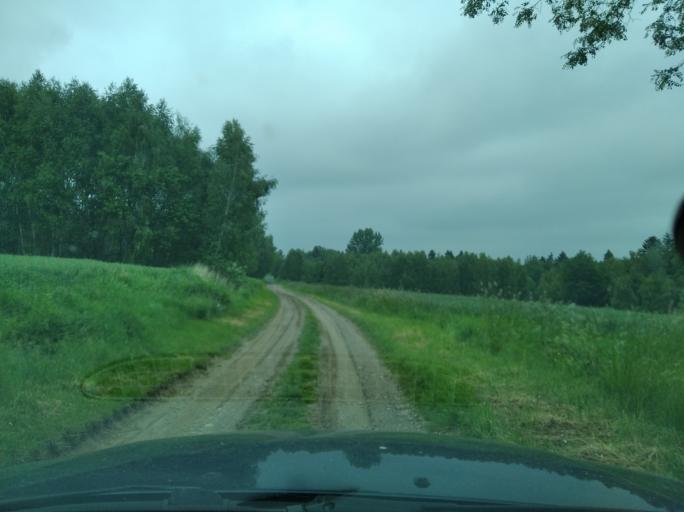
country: PL
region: Subcarpathian Voivodeship
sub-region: Powiat ropczycko-sedziszowski
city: Zagorzyce
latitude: 49.9820
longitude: 21.7081
